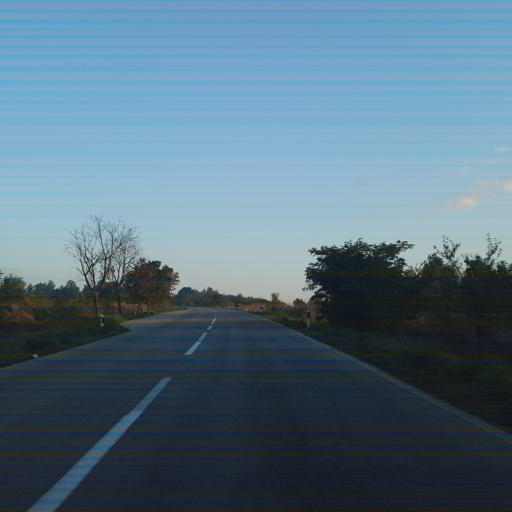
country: RS
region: Central Serbia
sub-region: Zajecarski Okrug
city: Zajecar
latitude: 44.0532
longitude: 22.3349
